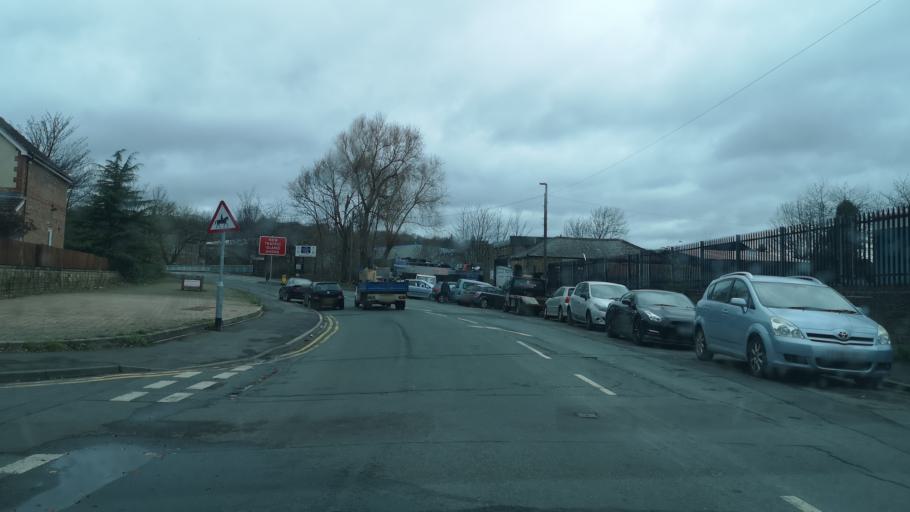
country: GB
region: England
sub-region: Kirklees
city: Dewsbury
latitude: 53.6817
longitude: -1.6389
